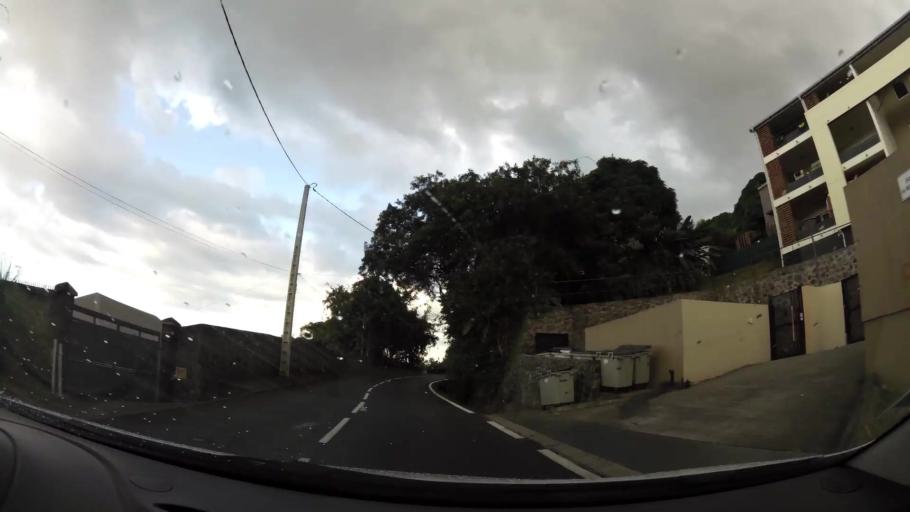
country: RE
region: Reunion
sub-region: Reunion
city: Saint-Denis
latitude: -20.9040
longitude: 55.4437
